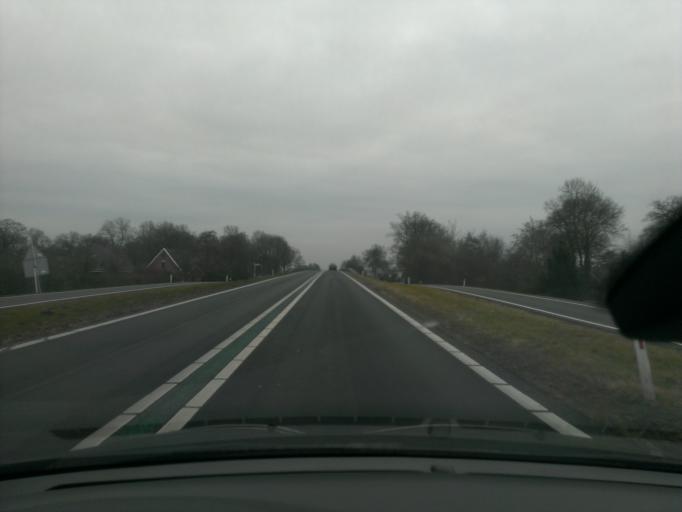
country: NL
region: Overijssel
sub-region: Gemeente Twenterand
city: Vriezenveen
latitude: 52.4171
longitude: 6.6328
